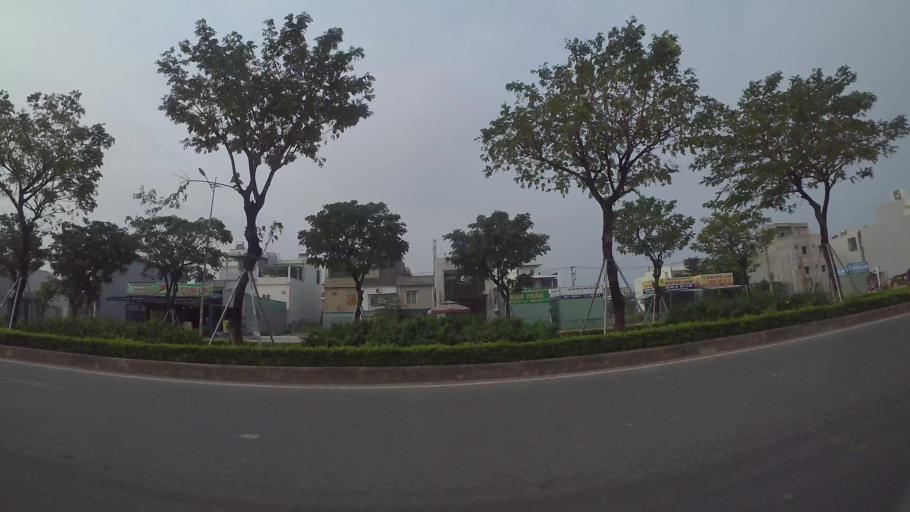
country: VN
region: Da Nang
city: Cam Le
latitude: 16.0205
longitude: 108.2276
